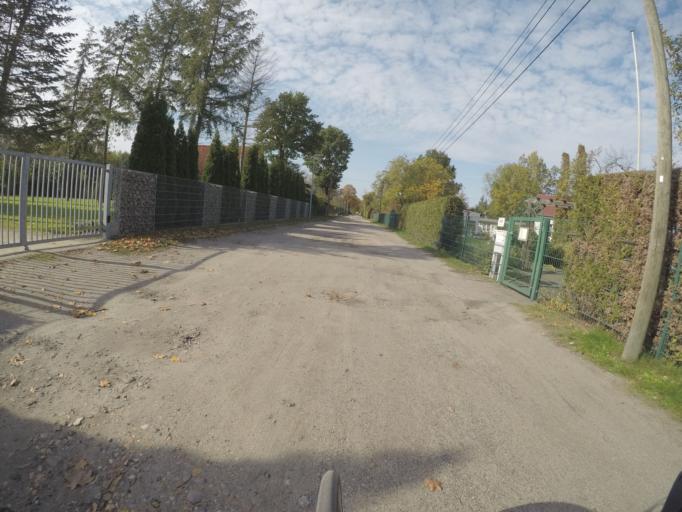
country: DE
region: Brandenburg
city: Leegebruch
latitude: 52.7450
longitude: 13.2084
